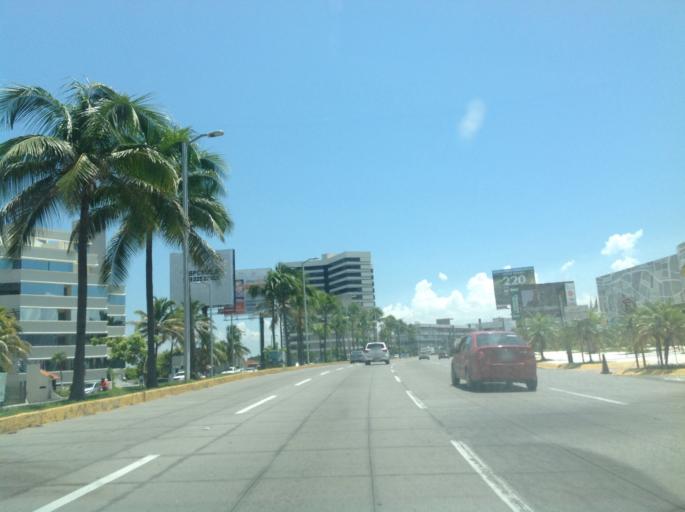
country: MX
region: Veracruz
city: Boca del Rio
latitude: 19.1387
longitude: -96.1036
